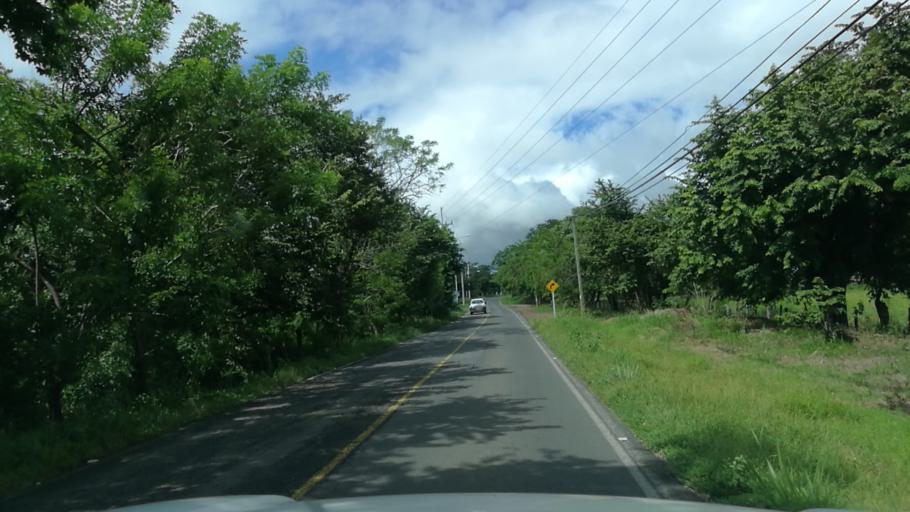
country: CR
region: Guanacaste
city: Bagaces
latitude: 10.5389
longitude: -85.2573
